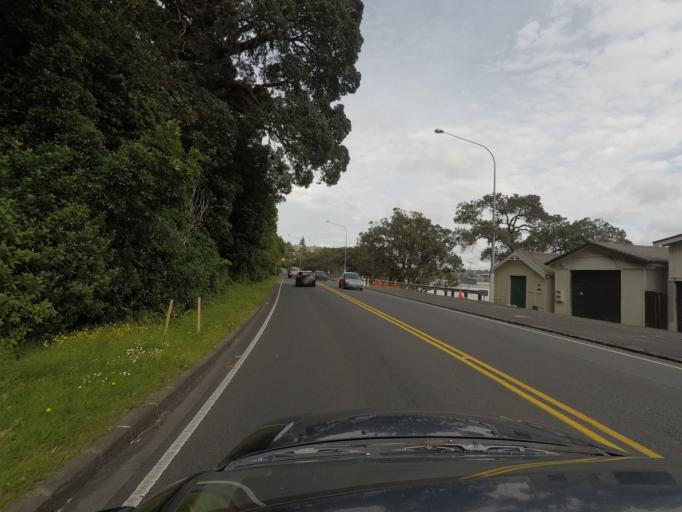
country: NZ
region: Auckland
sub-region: Auckland
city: Auckland
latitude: -36.8541
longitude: 174.8060
